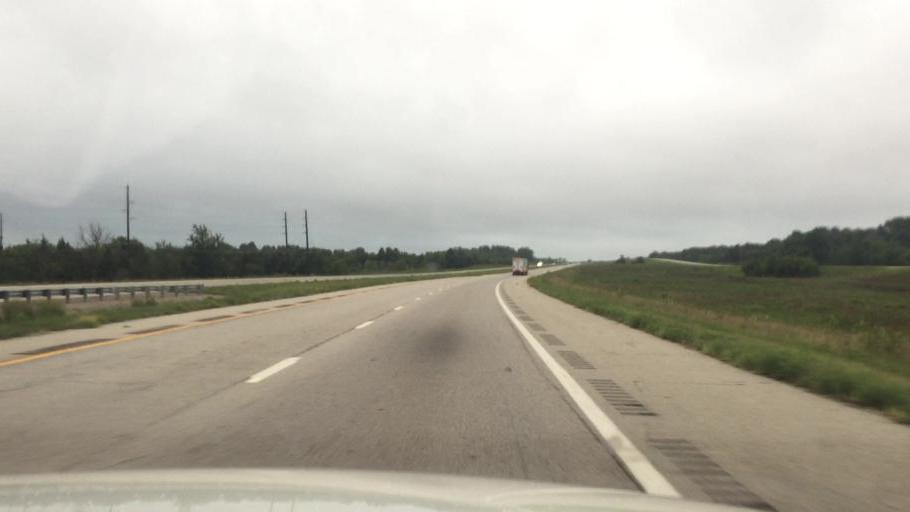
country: US
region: Kansas
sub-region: Montgomery County
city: Coffeyville
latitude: 37.0665
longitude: -95.5838
